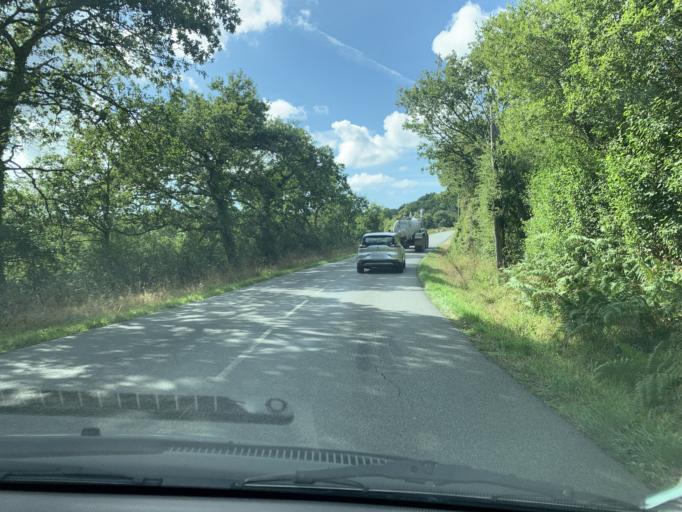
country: FR
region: Pays de la Loire
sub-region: Departement de la Loire-Atlantique
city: Asserac
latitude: 47.4086
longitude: -2.3609
